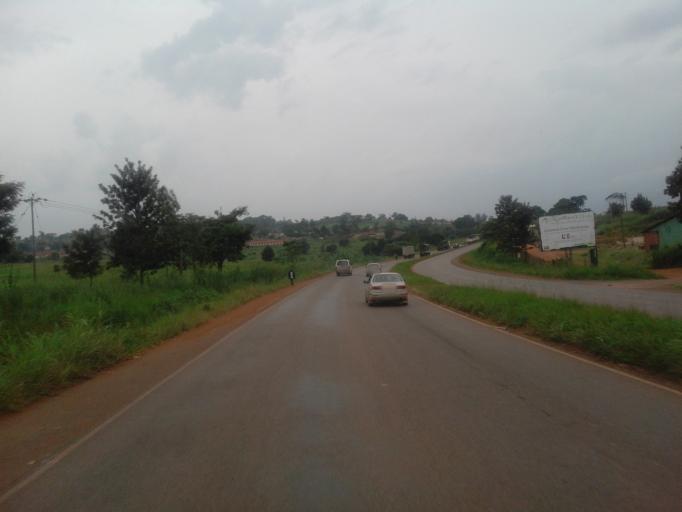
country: UG
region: Eastern Region
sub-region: Jinja District
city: Jinja
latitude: 0.4461
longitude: 33.1999
